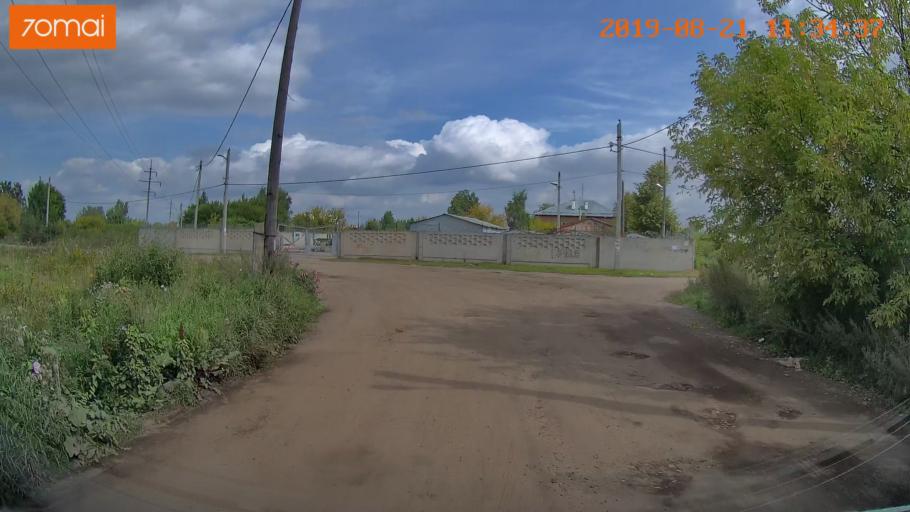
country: RU
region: Ivanovo
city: Novo-Talitsy
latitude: 56.9880
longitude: 40.9122
